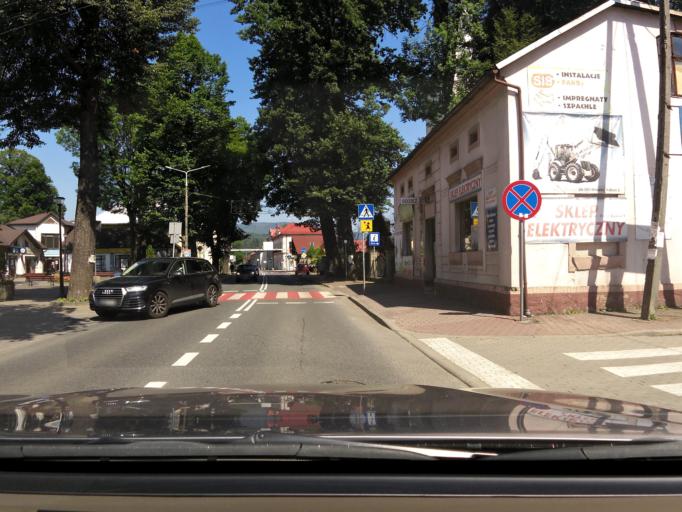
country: PL
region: Silesian Voivodeship
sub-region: Powiat zywiecki
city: Milowka
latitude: 49.5568
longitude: 19.0877
